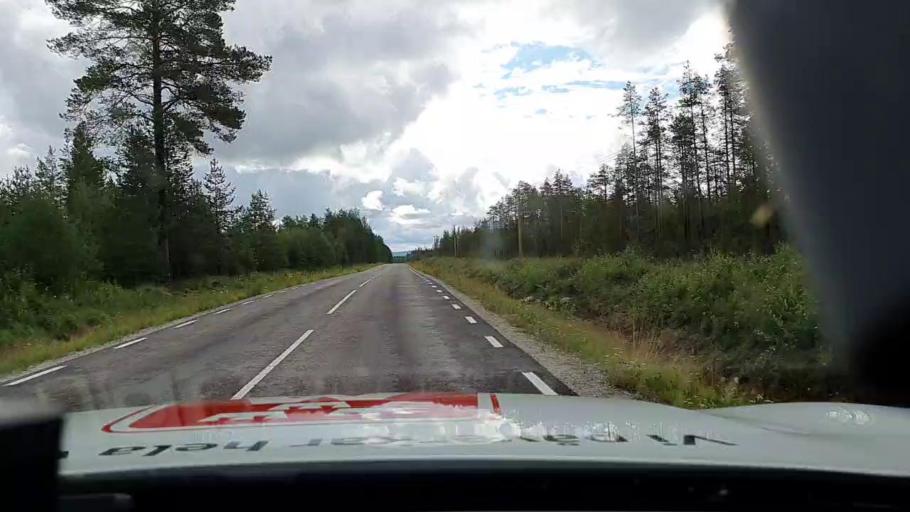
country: SE
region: Norrbotten
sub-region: Overkalix Kommun
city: OEverkalix
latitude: 66.2568
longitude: 22.8600
